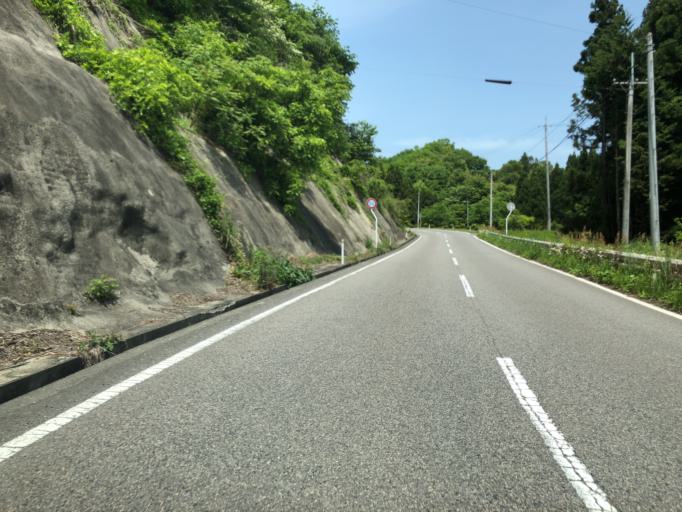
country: JP
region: Fukushima
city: Ishikawa
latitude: 37.1883
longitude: 140.4818
